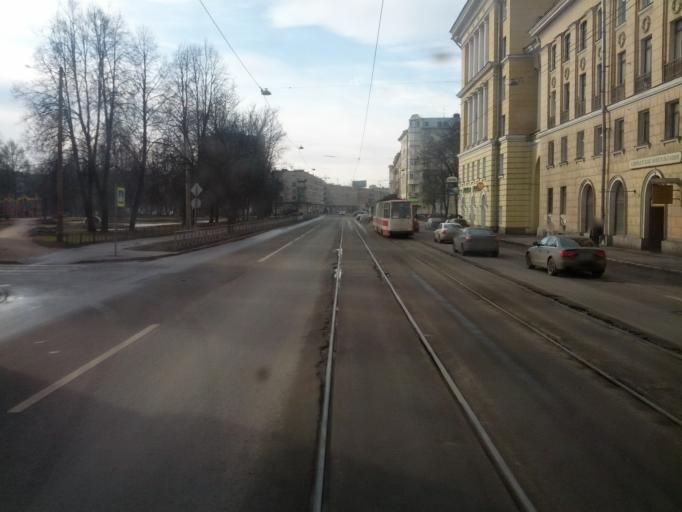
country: RU
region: Leningrad
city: Kalininskiy
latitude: 59.9491
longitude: 30.4146
